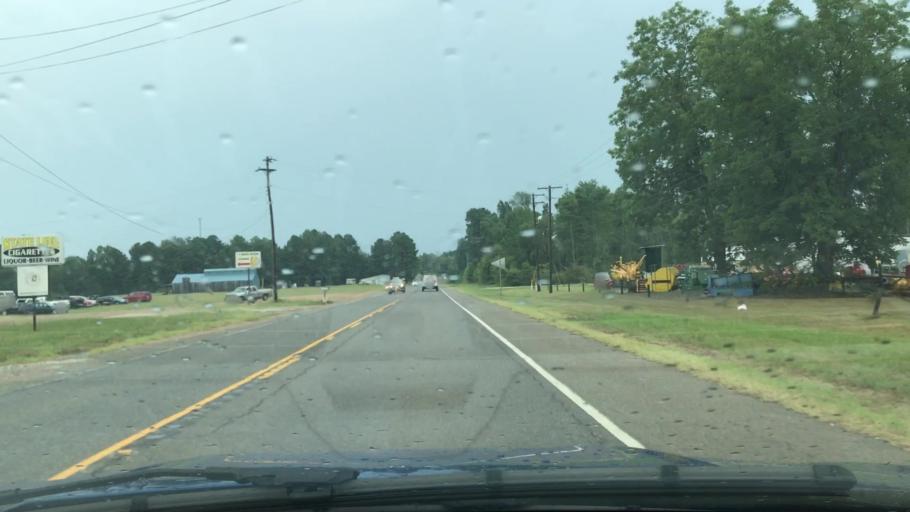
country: US
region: Texas
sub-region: Harrison County
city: Waskom
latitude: 32.4692
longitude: -94.0409
